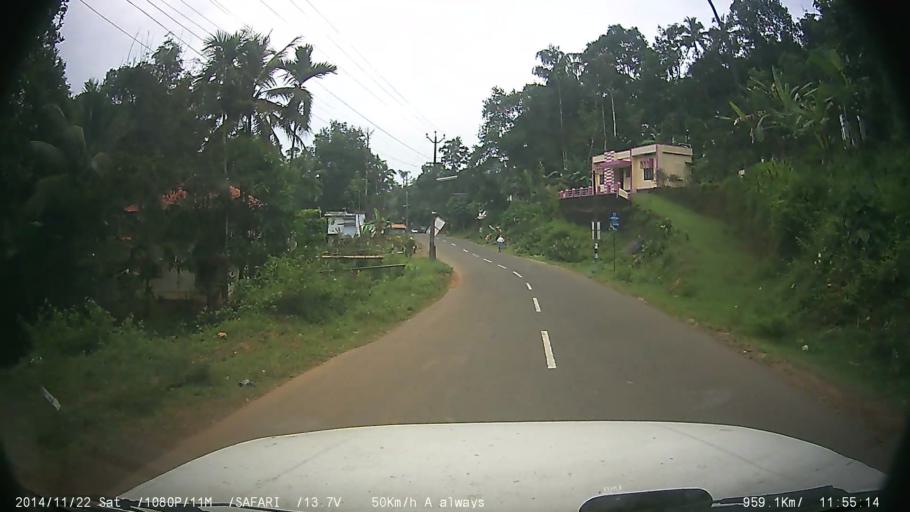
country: IN
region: Kerala
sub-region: Kottayam
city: Palackattumala
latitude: 9.8040
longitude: 76.5751
